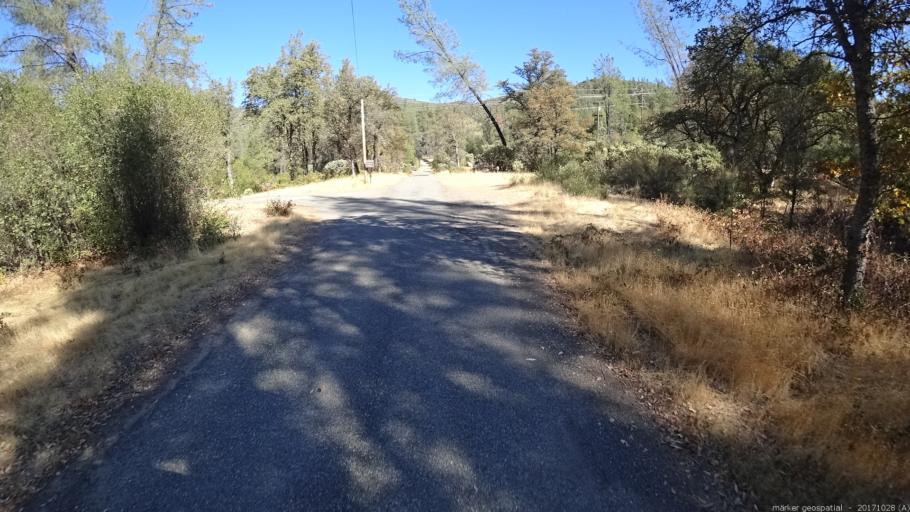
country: US
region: California
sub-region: Shasta County
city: Shasta
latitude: 40.6543
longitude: -122.5985
